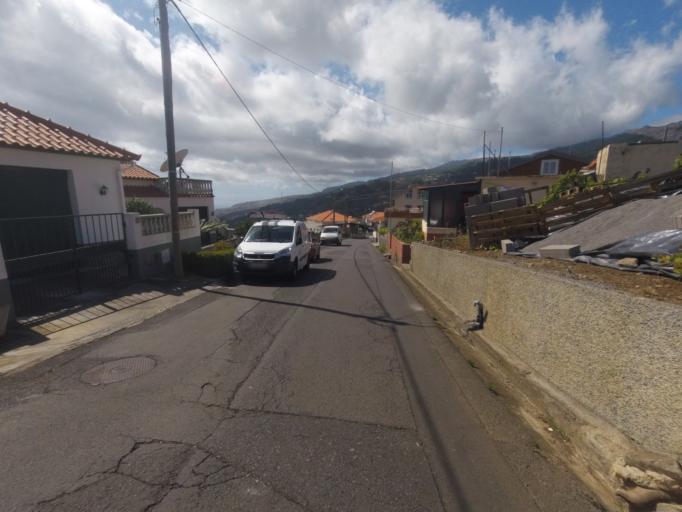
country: PT
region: Madeira
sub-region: Ribeira Brava
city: Campanario
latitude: 32.6802
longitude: -17.0427
